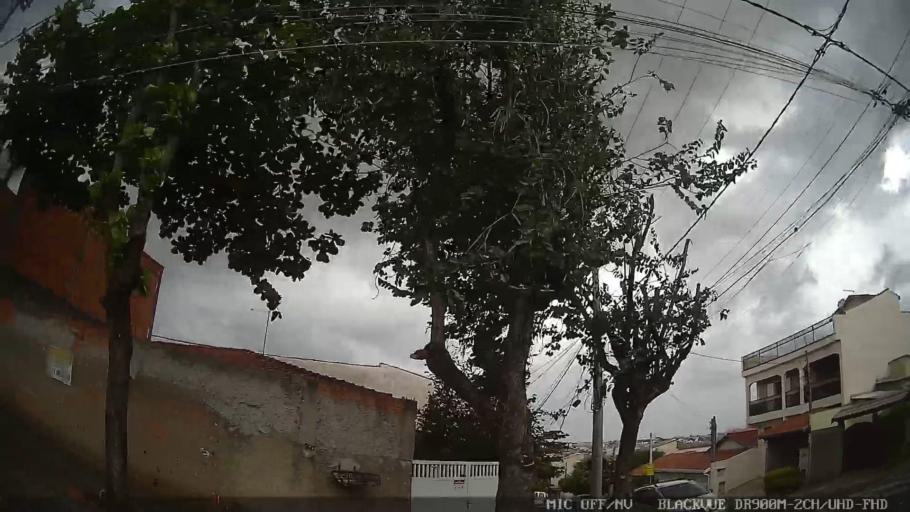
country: BR
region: Sao Paulo
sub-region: Indaiatuba
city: Indaiatuba
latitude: -23.1130
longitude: -47.2363
